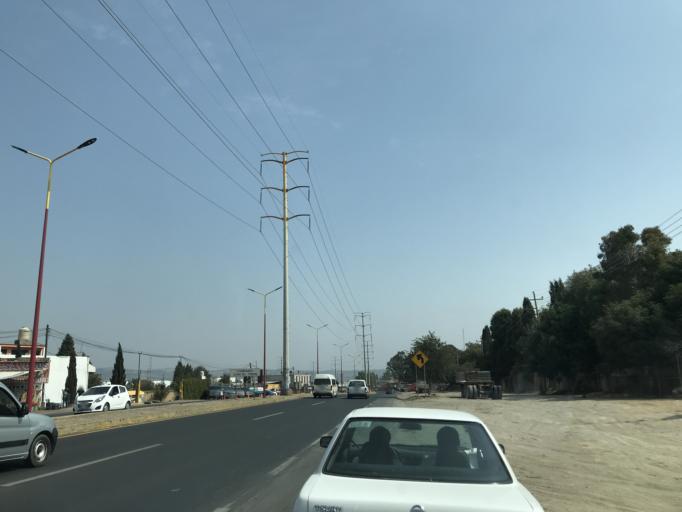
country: MX
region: Tlaxcala
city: La Magdalena Tlaltelulco
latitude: 19.2945
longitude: -98.1951
